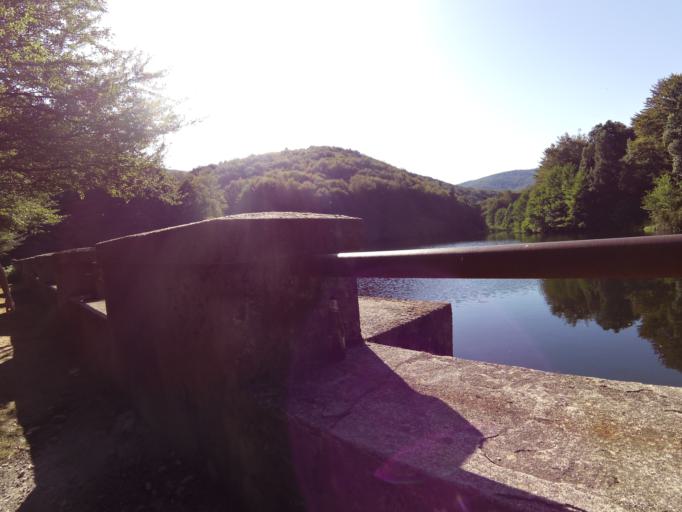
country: IT
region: Calabria
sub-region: Provincia di Vibo-Valentia
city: Nardodipace
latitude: 38.5122
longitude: 16.3690
